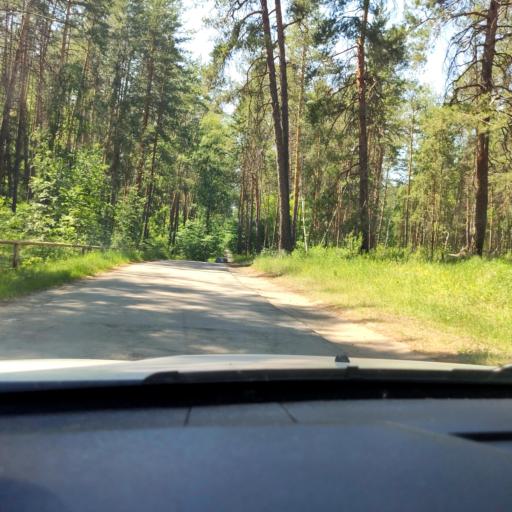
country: RU
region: Samara
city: Pribrezhnyy
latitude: 53.4773
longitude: 49.7914
